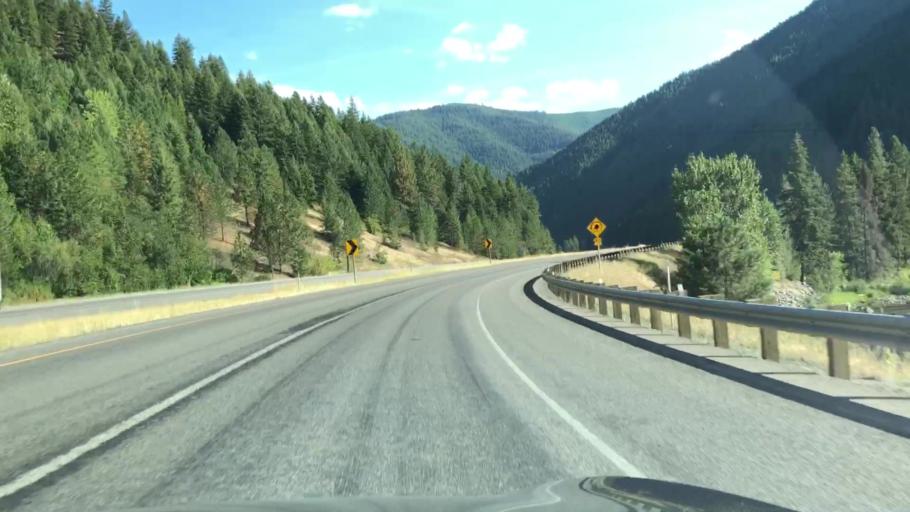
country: US
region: Montana
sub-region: Sanders County
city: Thompson Falls
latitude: 47.3265
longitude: -115.2506
